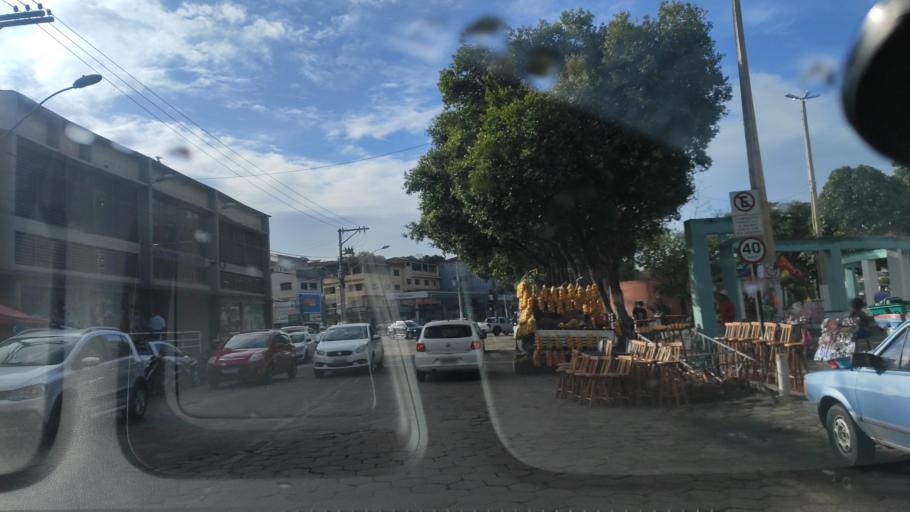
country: BR
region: Espirito Santo
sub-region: Nova Venecia
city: Nova Venecia
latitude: -18.7081
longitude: -40.4000
